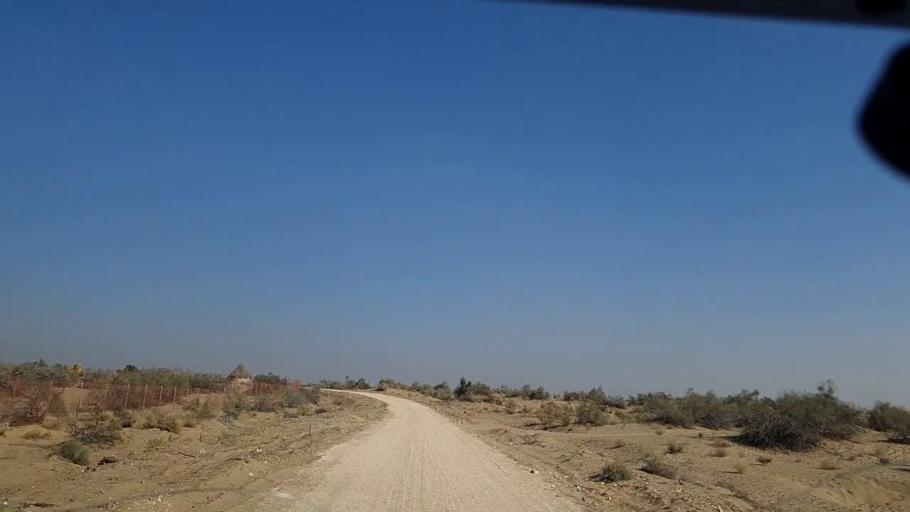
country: PK
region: Sindh
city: Khanpur
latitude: 27.5585
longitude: 69.3997
